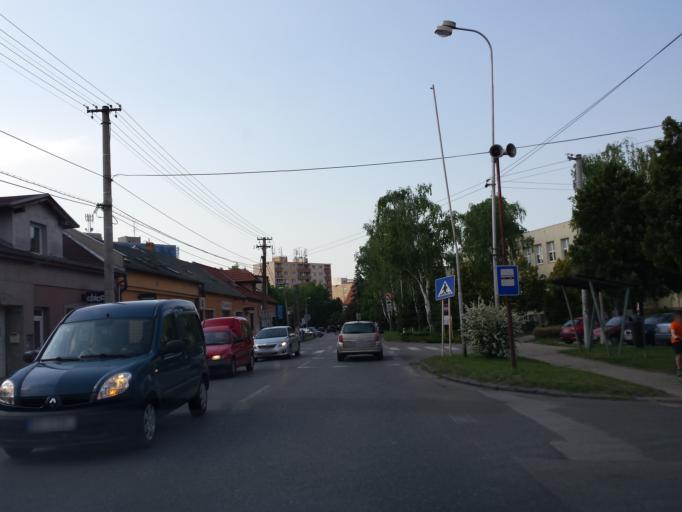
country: SK
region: Bratislavsky
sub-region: Okres Malacky
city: Malacky
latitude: 48.4329
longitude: 17.0185
